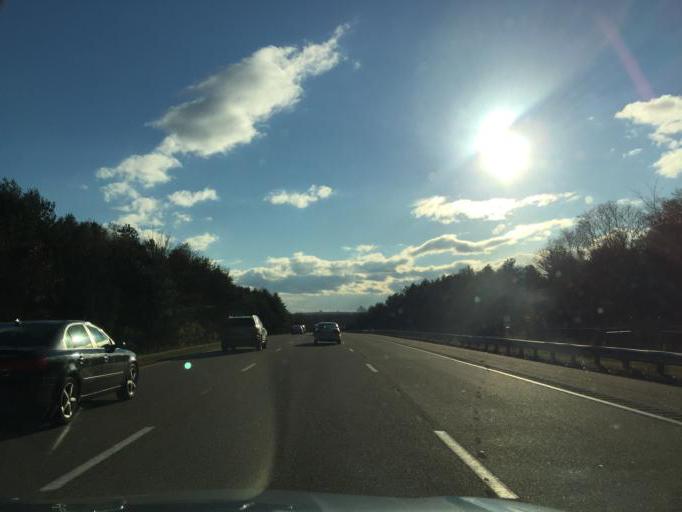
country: US
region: Massachusetts
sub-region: Bristol County
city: North Seekonk
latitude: 41.9182
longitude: -71.3331
